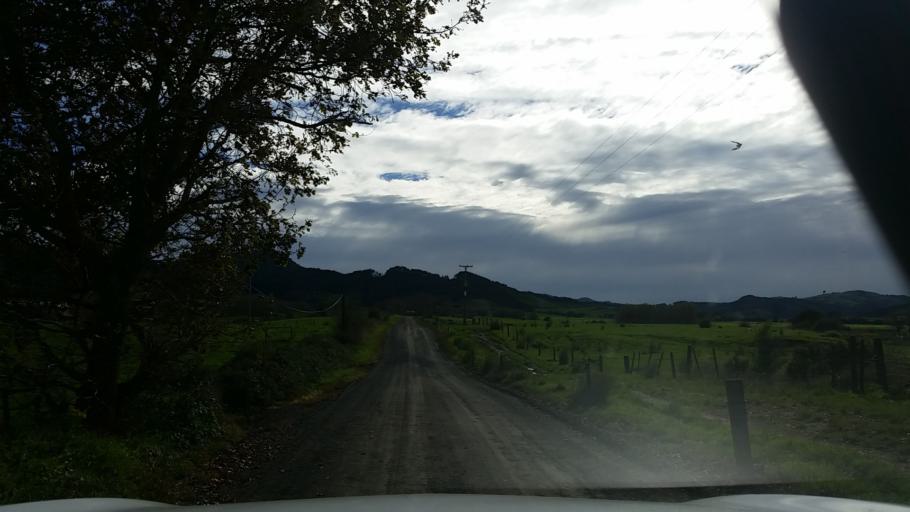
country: NZ
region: Waikato
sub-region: Hauraki District
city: Ngatea
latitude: -37.5120
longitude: 175.4089
